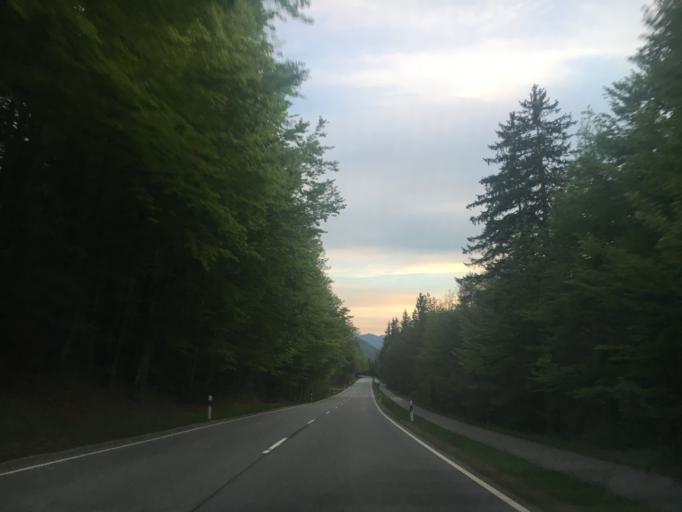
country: DE
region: Bavaria
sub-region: Upper Bavaria
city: Lenggries
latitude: 47.6201
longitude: 11.5939
